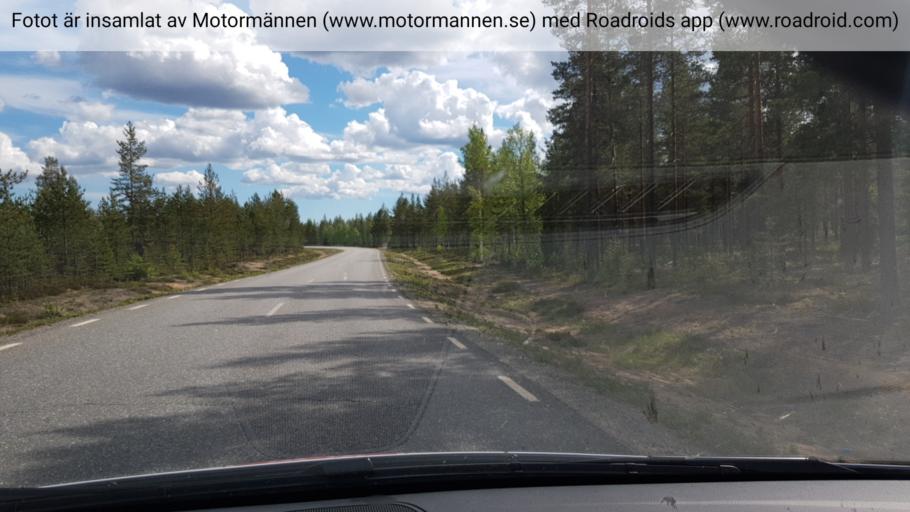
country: SE
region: Vaesterbotten
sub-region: Umea Kommun
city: Ersmark
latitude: 64.1786
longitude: 20.3434
